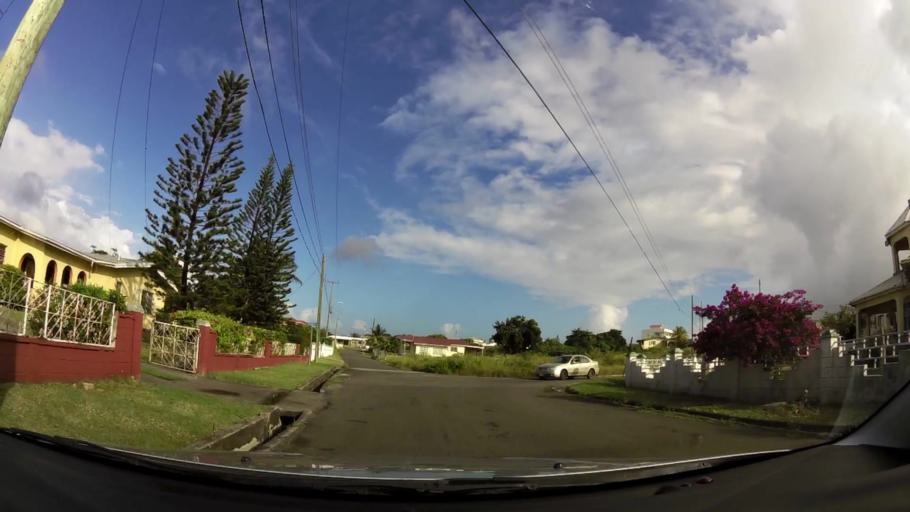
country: AG
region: Saint John
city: Saint John's
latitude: 17.1288
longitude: -61.8333
